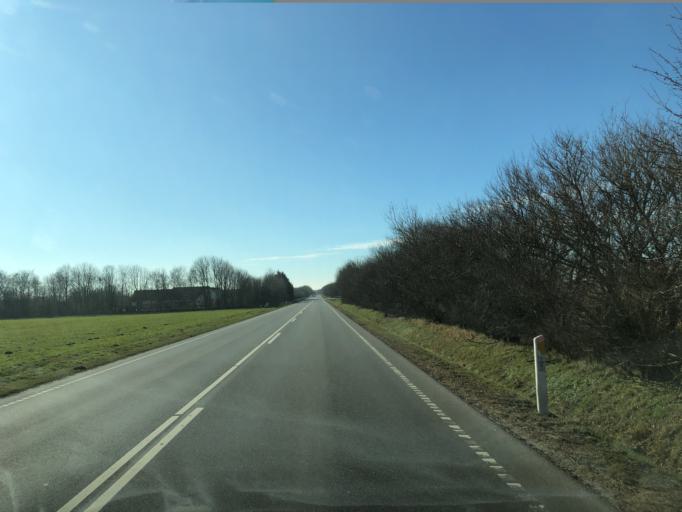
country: DK
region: Central Jutland
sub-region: Ikast-Brande Kommune
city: Bording Kirkeby
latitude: 56.1509
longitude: 9.2283
